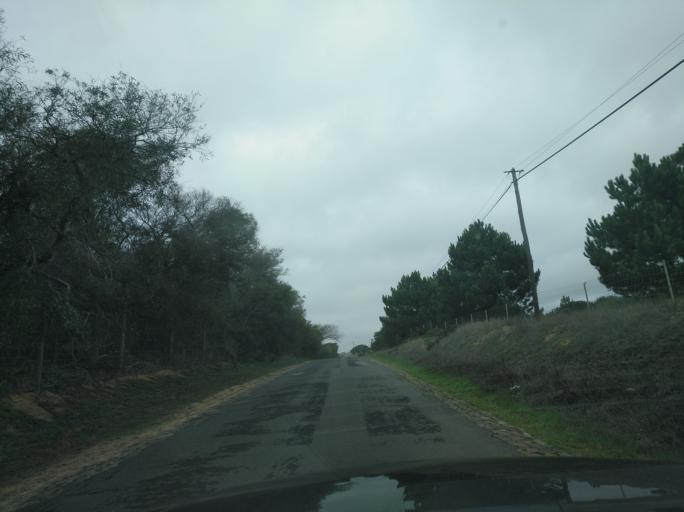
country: PT
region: Setubal
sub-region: Sines
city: Porto Covo
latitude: 37.8332
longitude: -8.7869
